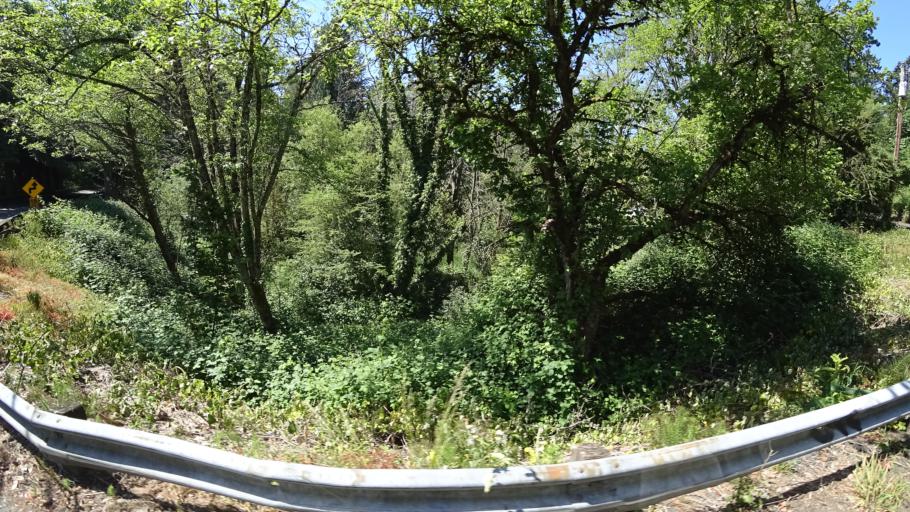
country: US
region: Oregon
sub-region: Clackamas County
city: Happy Valley
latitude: 45.4726
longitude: -122.5243
